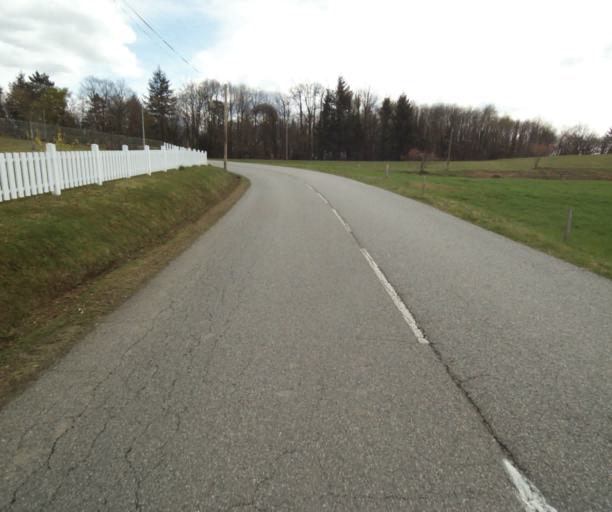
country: FR
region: Limousin
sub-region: Departement de la Correze
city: Laguenne
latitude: 45.2097
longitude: 1.8677
